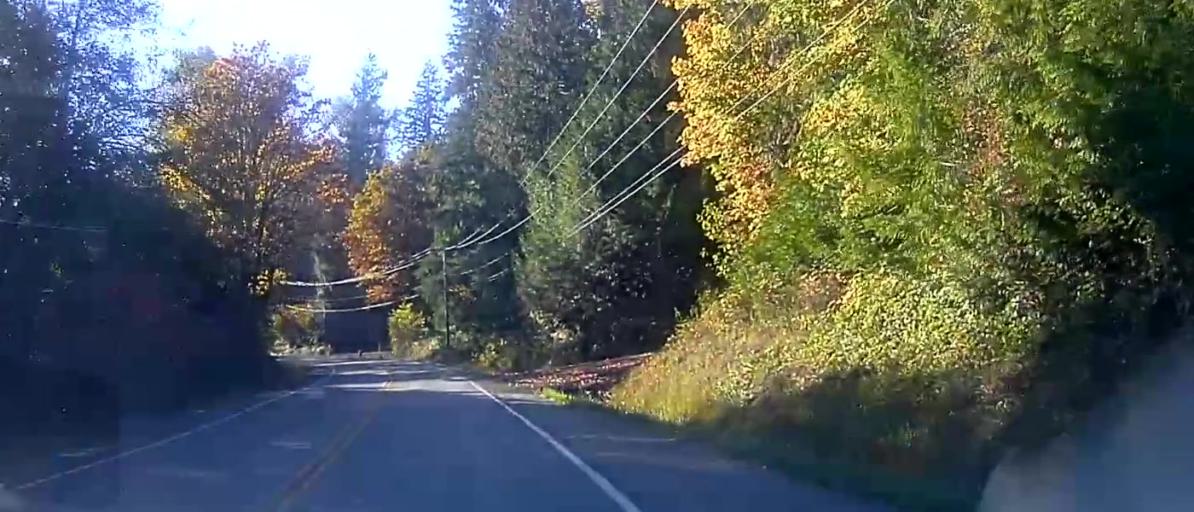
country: US
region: Washington
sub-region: Skagit County
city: Big Lake
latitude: 48.4213
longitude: -122.2602
